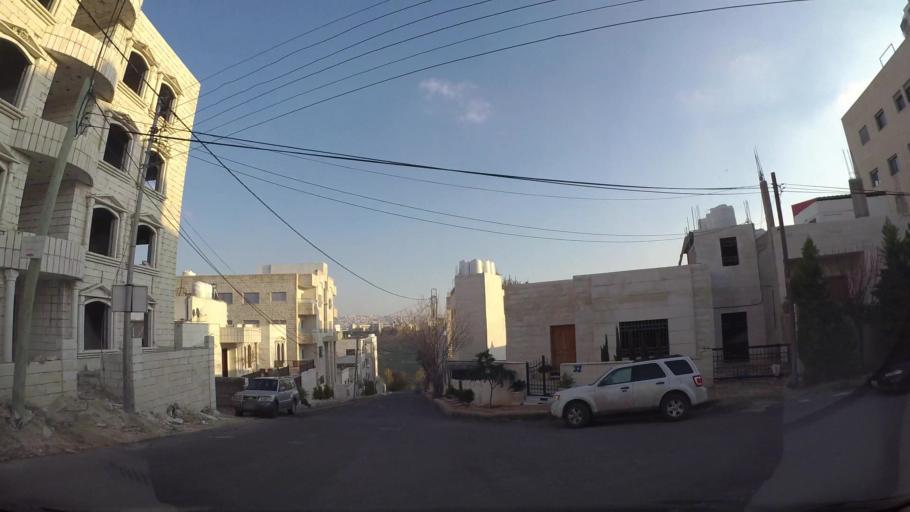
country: JO
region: Amman
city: Amman
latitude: 31.9843
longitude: 35.9626
